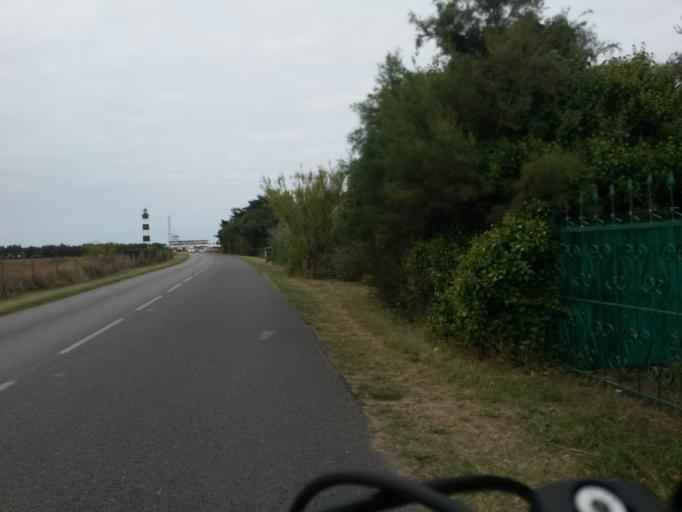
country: FR
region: Poitou-Charentes
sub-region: Departement de la Charente-Maritime
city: Saint-Denis-d'Oleron
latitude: 46.0452
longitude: -1.4024
